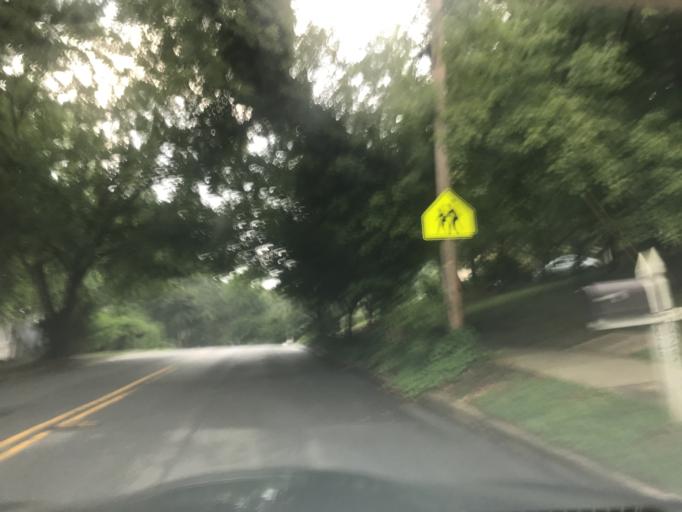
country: US
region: North Carolina
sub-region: Wake County
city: West Raleigh
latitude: 35.8434
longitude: -78.6576
